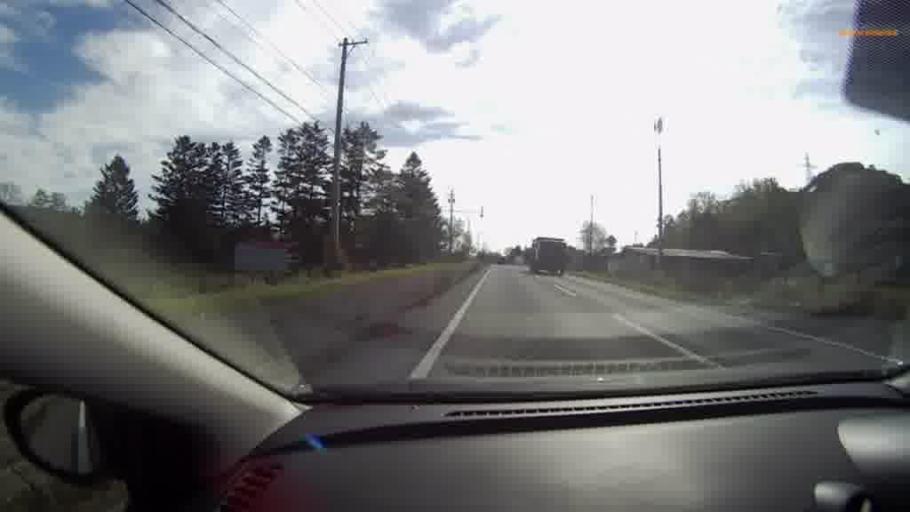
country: JP
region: Hokkaido
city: Kushiro
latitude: 43.0857
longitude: 144.1348
